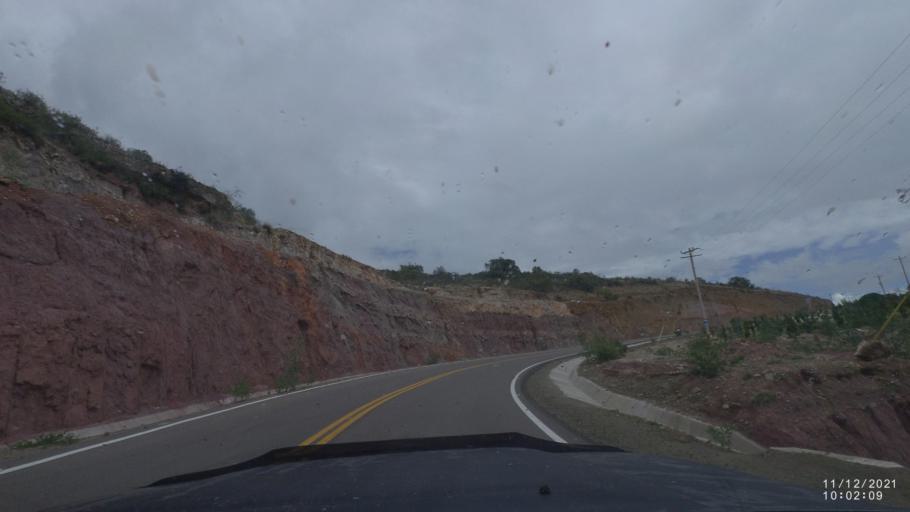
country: BO
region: Cochabamba
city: Cliza
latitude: -17.7226
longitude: -65.9318
